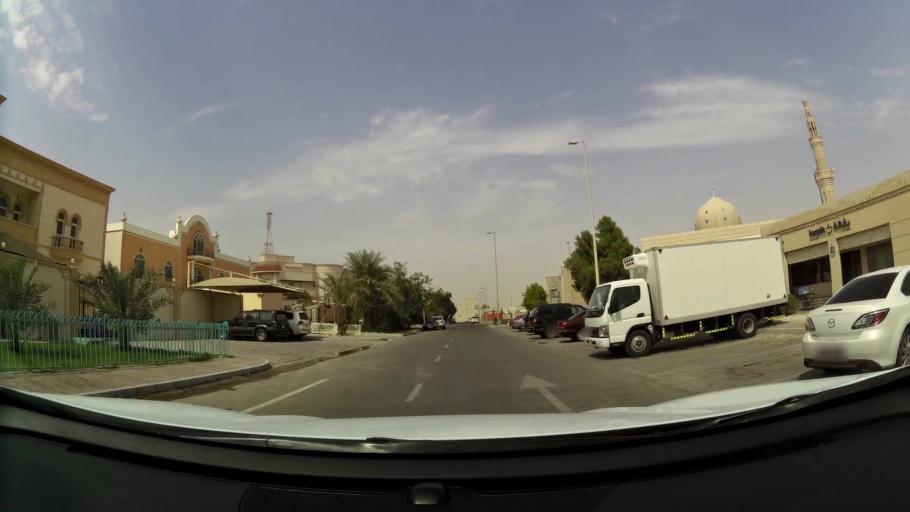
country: AE
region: Abu Dhabi
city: Abu Dhabi
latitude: 24.3117
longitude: 54.6092
